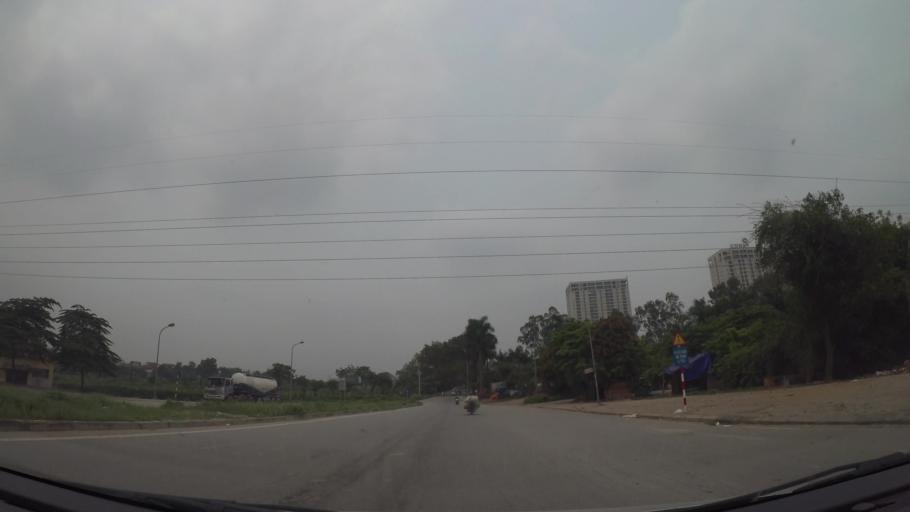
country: VN
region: Ha Noi
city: Cau Dien
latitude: 21.0131
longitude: 105.7464
